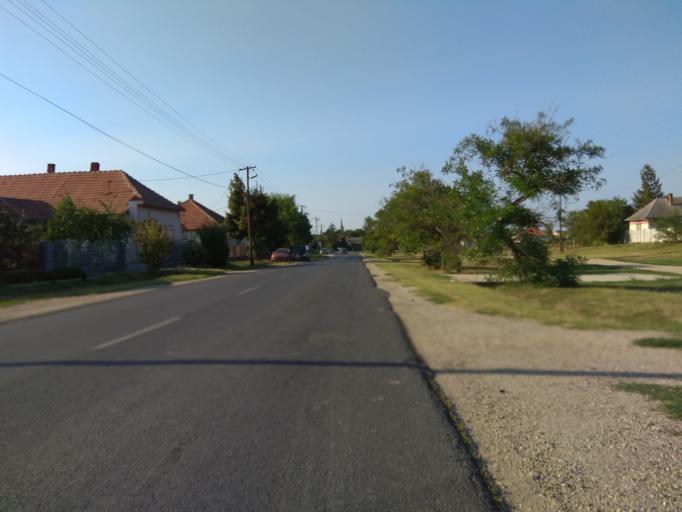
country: HU
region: Borsod-Abauj-Zemplen
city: Onod
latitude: 47.9977
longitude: 20.9203
